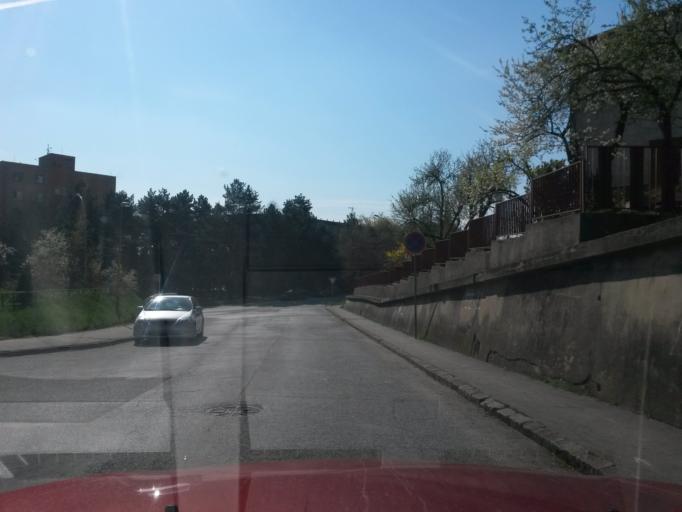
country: SK
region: Kosicky
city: Kosice
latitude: 48.7518
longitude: 21.2434
